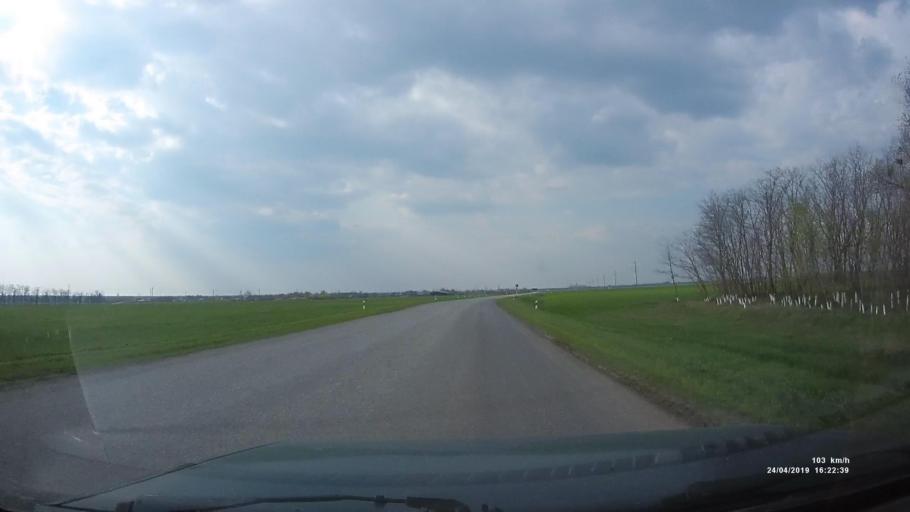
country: RU
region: Rostov
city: Orlovskiy
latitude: 46.8227
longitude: 42.0545
